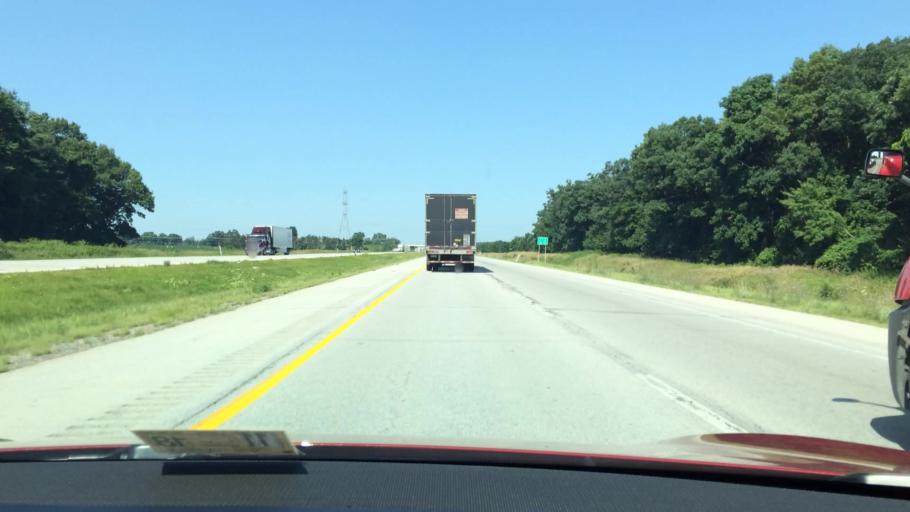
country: US
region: Indiana
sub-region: Elkhart County
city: Bristol
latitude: 41.7313
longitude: -85.8593
